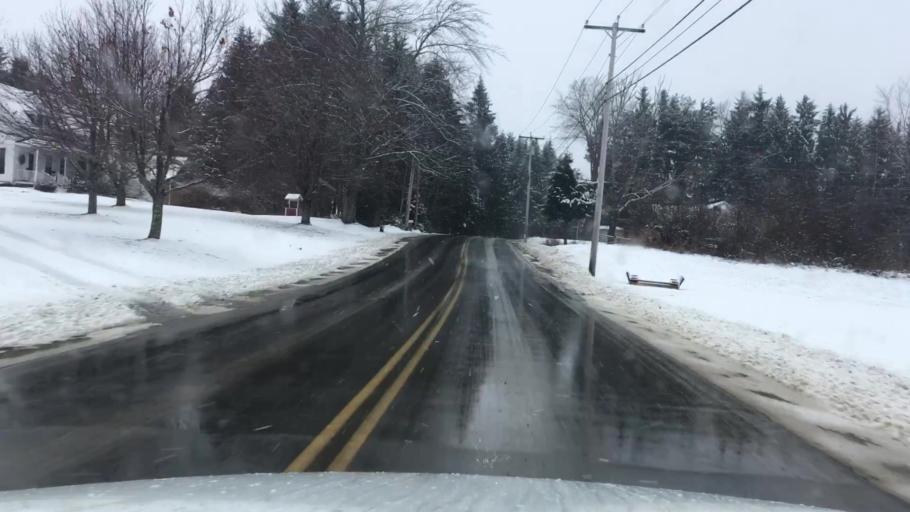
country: US
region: Maine
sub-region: Knox County
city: Warren
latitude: 44.1223
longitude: -69.2529
